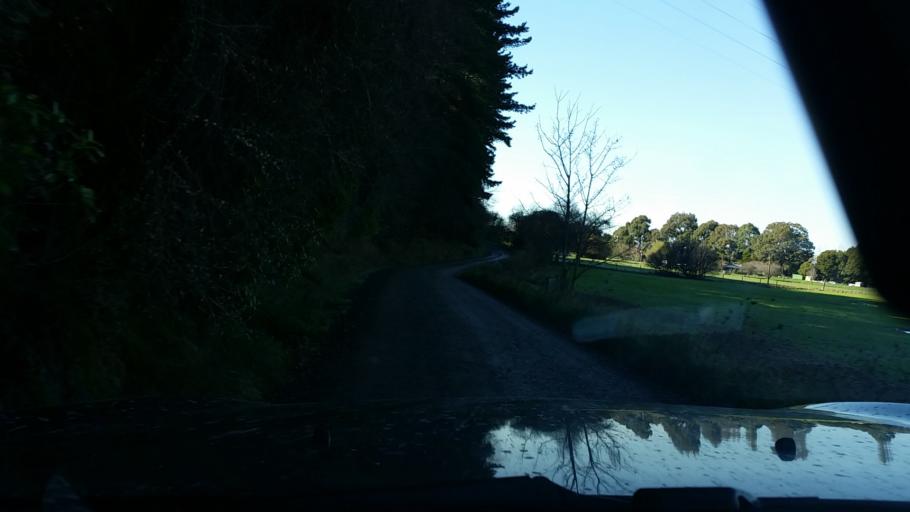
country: NZ
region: Marlborough
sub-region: Marlborough District
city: Blenheim
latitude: -41.4631
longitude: 173.7920
